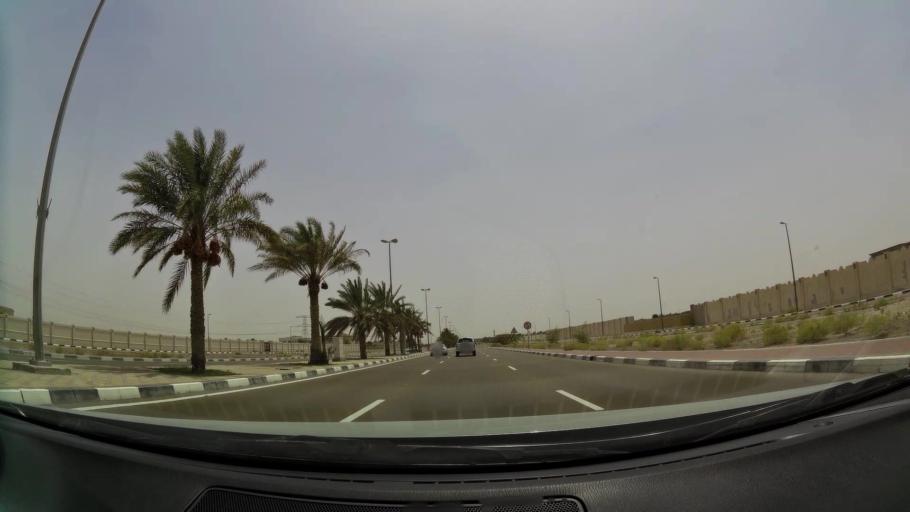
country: AE
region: Abu Dhabi
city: Al Ain
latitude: 24.1874
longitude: 55.6859
